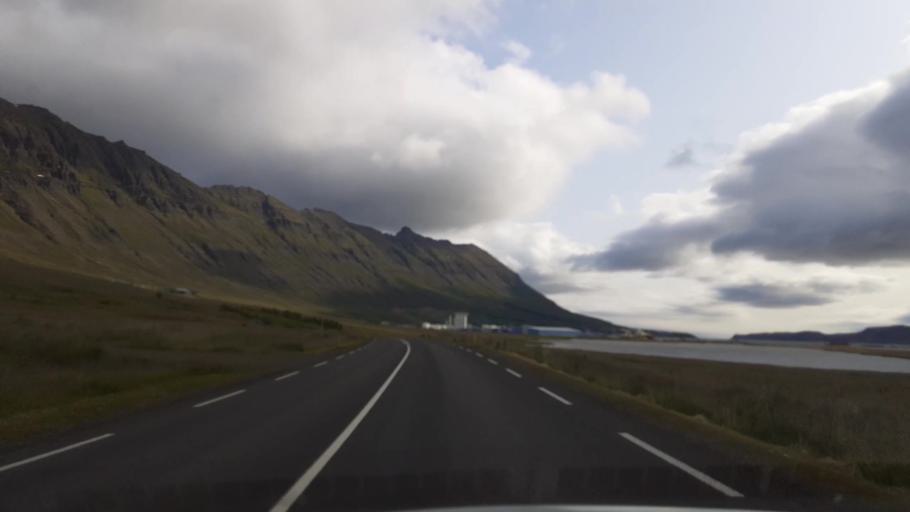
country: IS
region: East
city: Neskaupstadur
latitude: 65.1305
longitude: -13.7643
